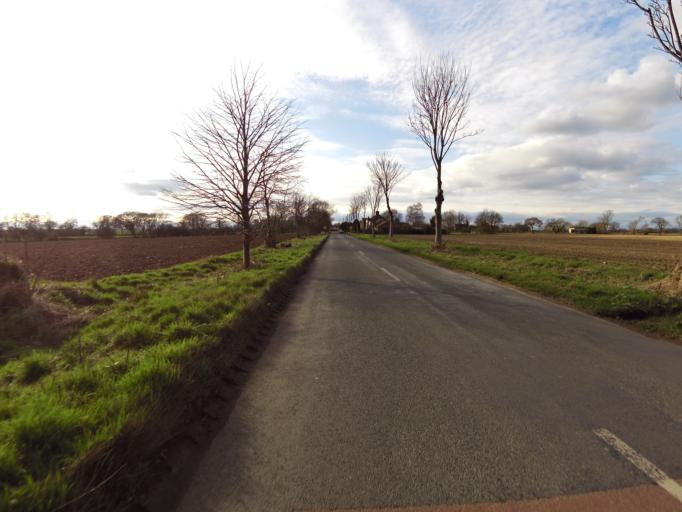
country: GB
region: England
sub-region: East Riding of Yorkshire
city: Pollington
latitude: 53.7116
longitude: -1.0675
